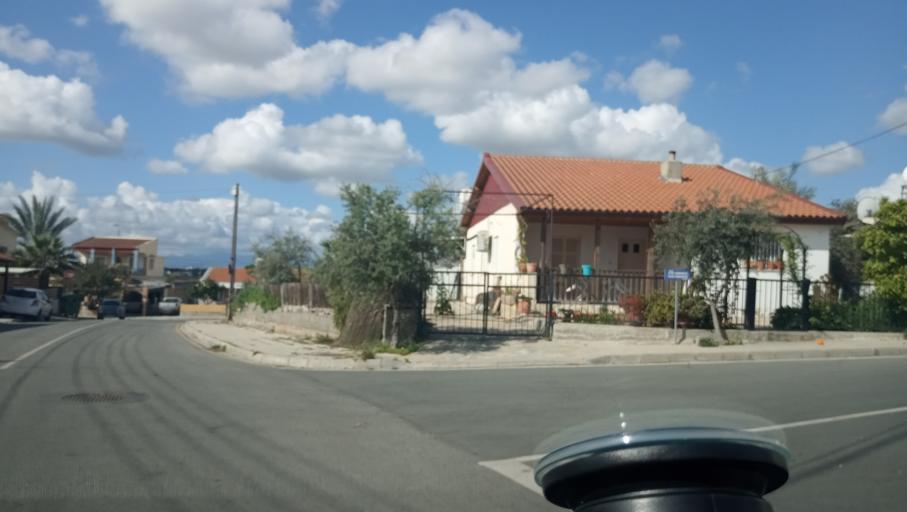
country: CY
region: Lefkosia
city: Geri
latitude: 35.1000
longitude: 33.4078
